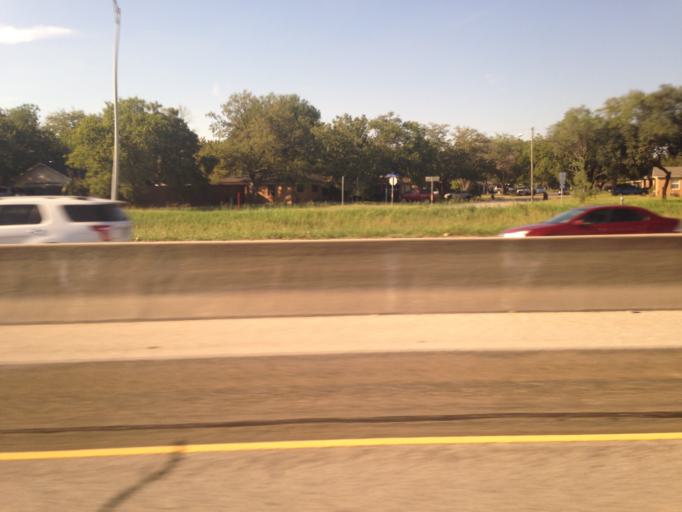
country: US
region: Texas
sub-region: Tarrant County
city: Richland Hills
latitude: 32.7987
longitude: -97.2269
